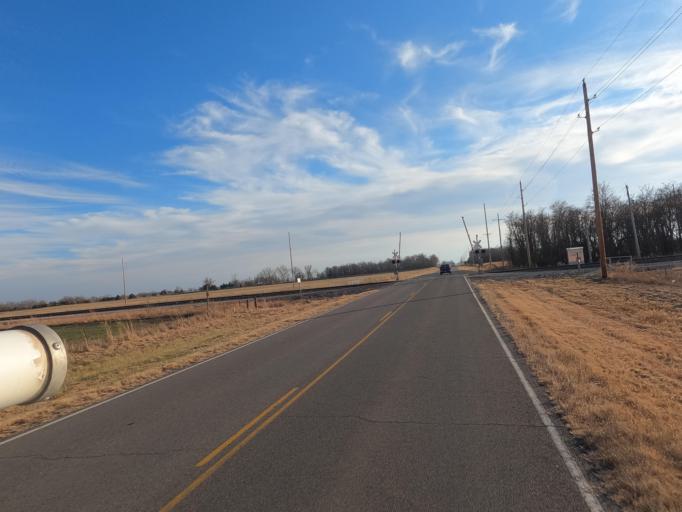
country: US
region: Kansas
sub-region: Reno County
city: Buhler
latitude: 38.0371
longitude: -97.7753
